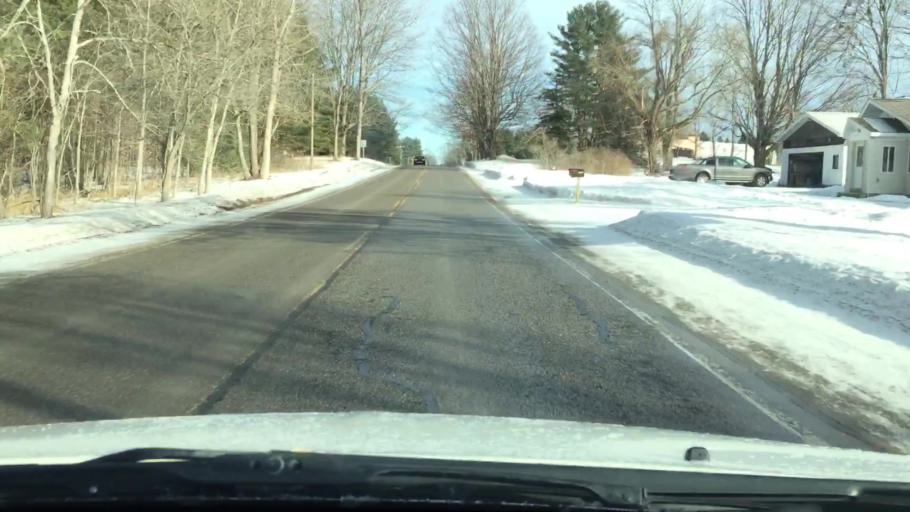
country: US
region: Michigan
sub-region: Kalkaska County
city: Kalkaska
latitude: 44.6412
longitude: -85.2671
